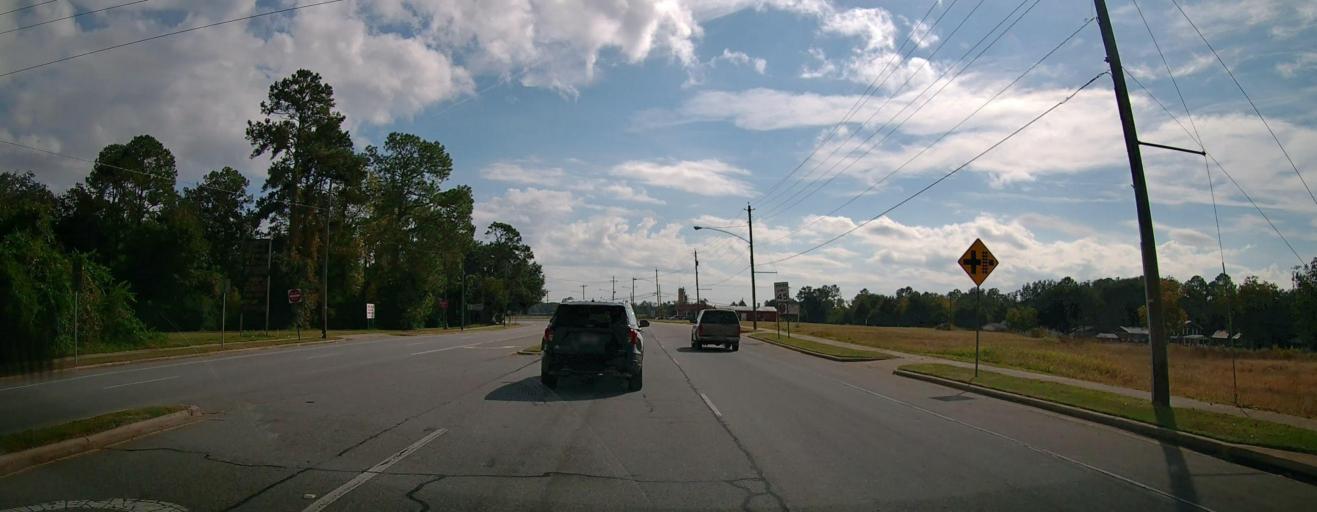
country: US
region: Georgia
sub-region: Mitchell County
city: Camilla
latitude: 31.2297
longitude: -84.2000
